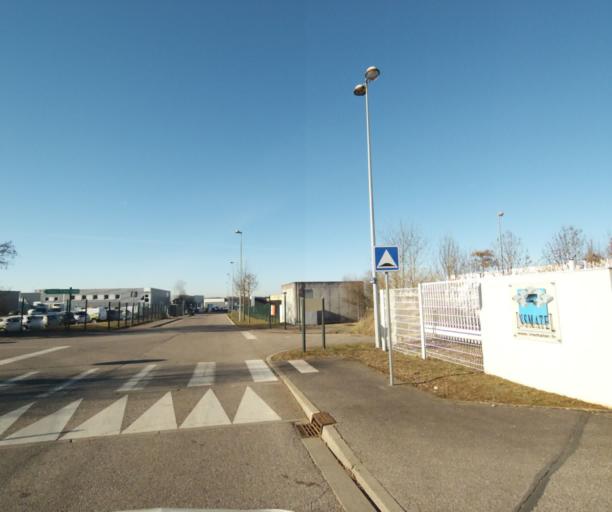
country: FR
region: Lorraine
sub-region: Departement de Meurthe-et-Moselle
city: Laxou
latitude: 48.7032
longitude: 6.1265
